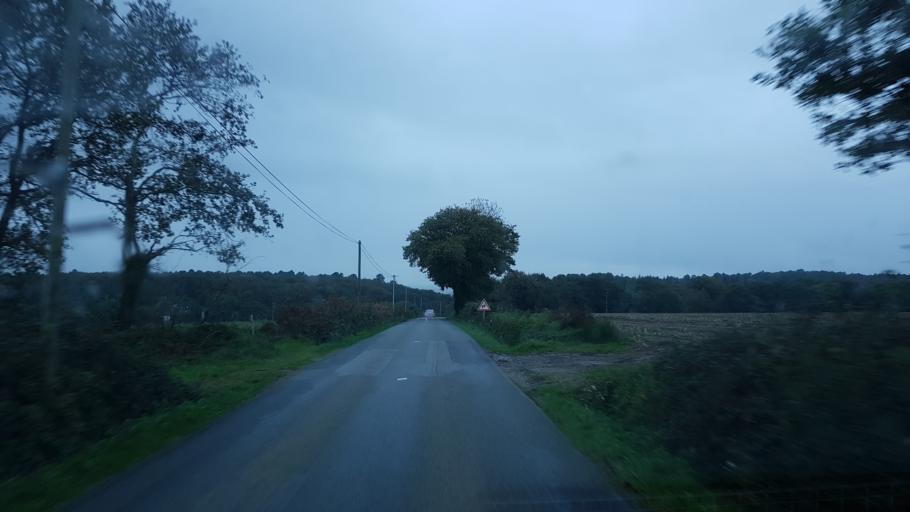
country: FR
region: Brittany
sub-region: Departement du Morbihan
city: Trefflean
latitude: 47.6733
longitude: -2.6094
